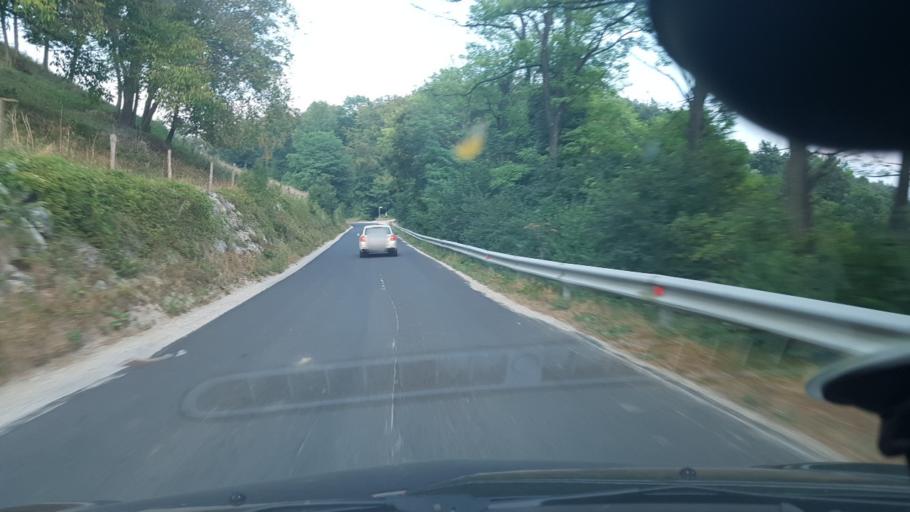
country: SI
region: Kozje
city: Kozje
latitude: 46.1053
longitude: 15.5900
